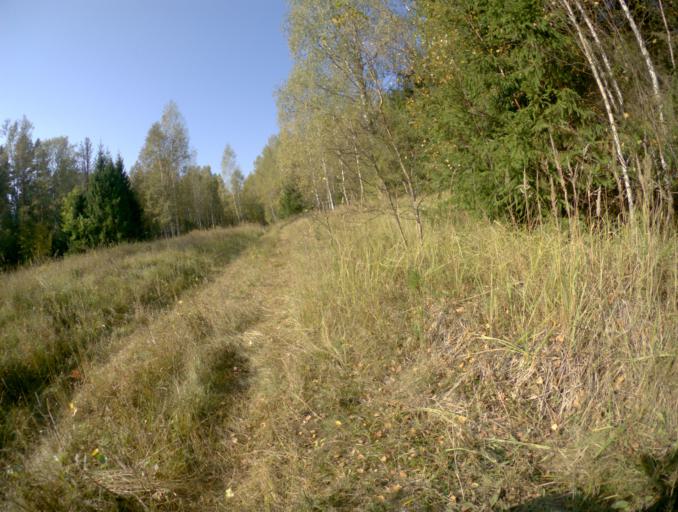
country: RU
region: Ivanovo
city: Lezhnevo
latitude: 56.5593
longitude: 40.7685
